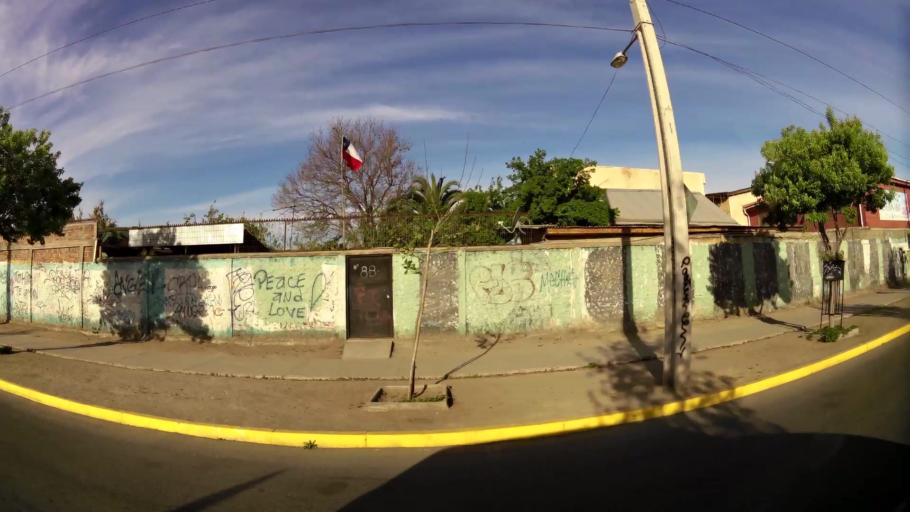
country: CL
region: Santiago Metropolitan
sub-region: Provincia de Cordillera
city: Puente Alto
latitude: -33.6138
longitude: -70.5771
